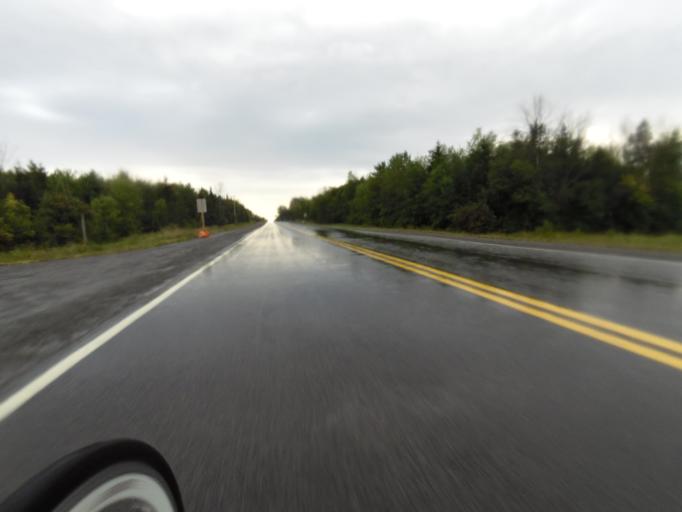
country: CA
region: Ontario
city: Bells Corners
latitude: 45.1887
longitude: -75.7243
